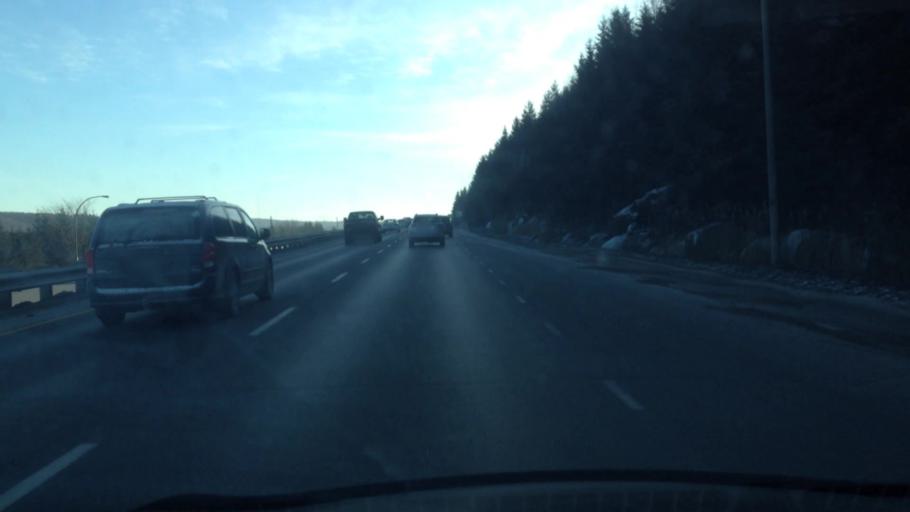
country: CA
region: Quebec
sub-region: Laurentides
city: Prevost
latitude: 45.8819
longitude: -74.1026
